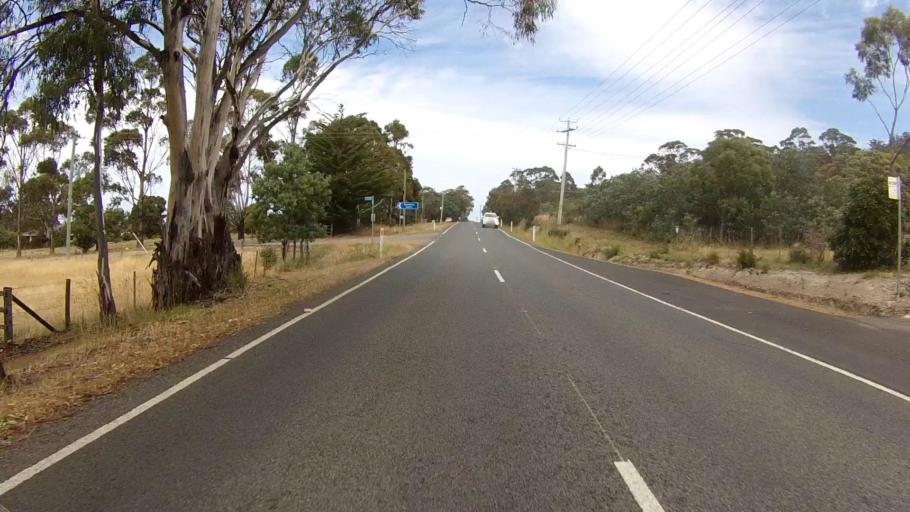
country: AU
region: Tasmania
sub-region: Clarence
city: Acton Park
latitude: -42.8952
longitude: 147.4813
